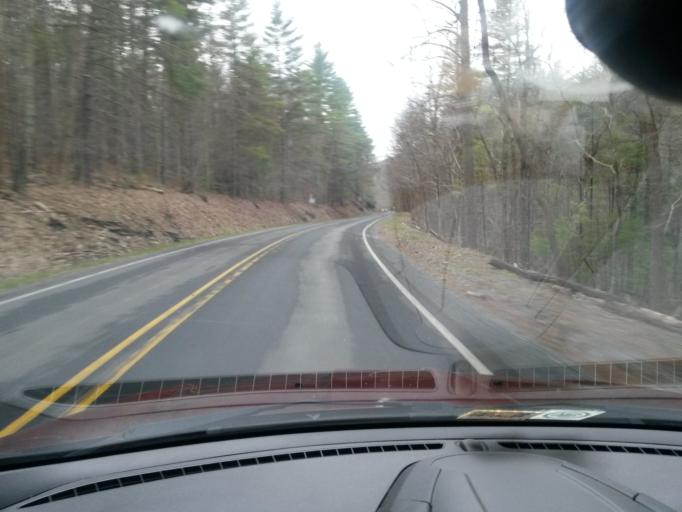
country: US
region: Virginia
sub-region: Bath County
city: Warm Springs
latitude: 38.1094
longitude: -79.7655
